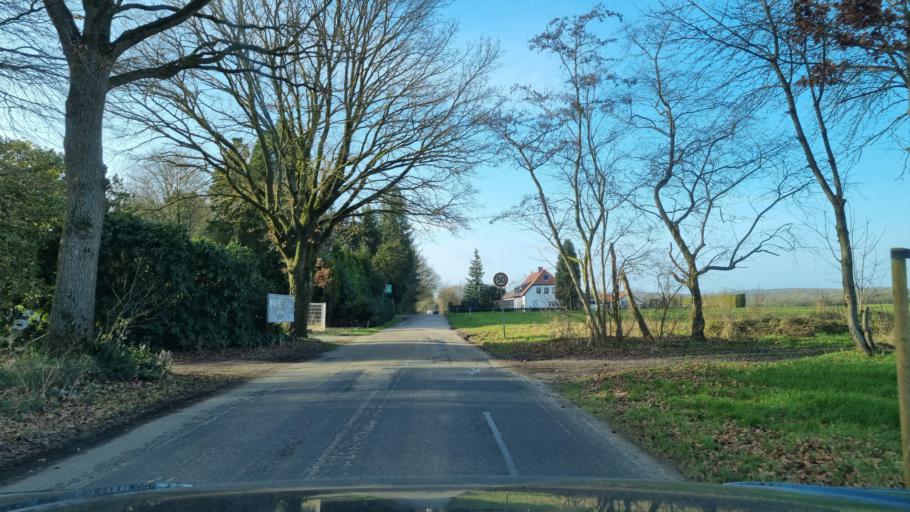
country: DE
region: North Rhine-Westphalia
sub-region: Regierungsbezirk Dusseldorf
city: Kleve
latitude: 51.7483
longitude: 6.1202
